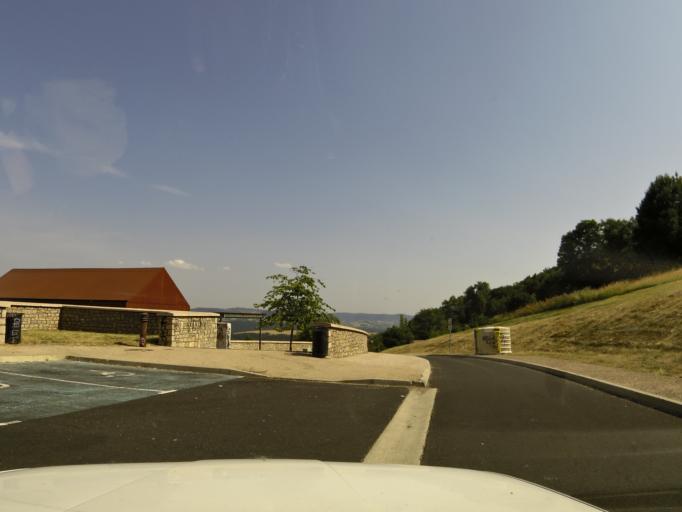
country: FR
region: Languedoc-Roussillon
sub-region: Departement de la Lozere
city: Marvejols
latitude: 44.5665
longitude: 3.2516
